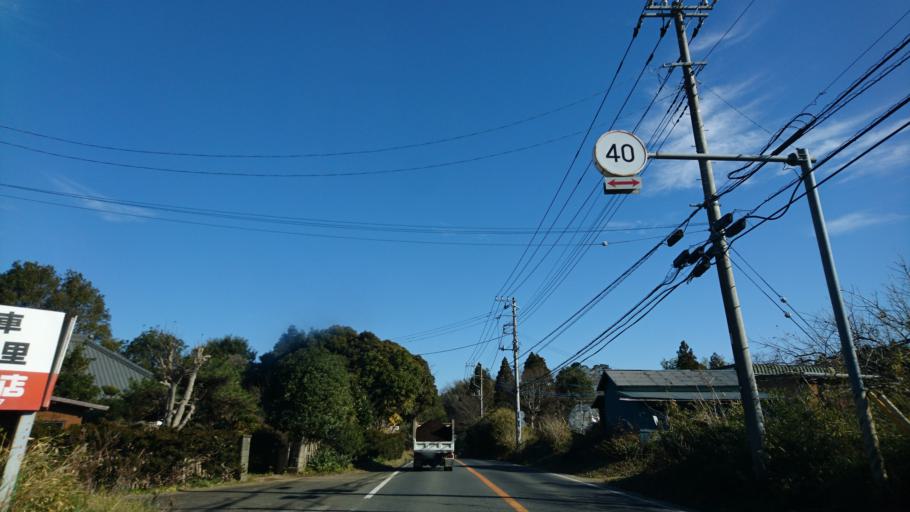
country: JP
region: Chiba
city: Yachimata
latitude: 35.6222
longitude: 140.3207
